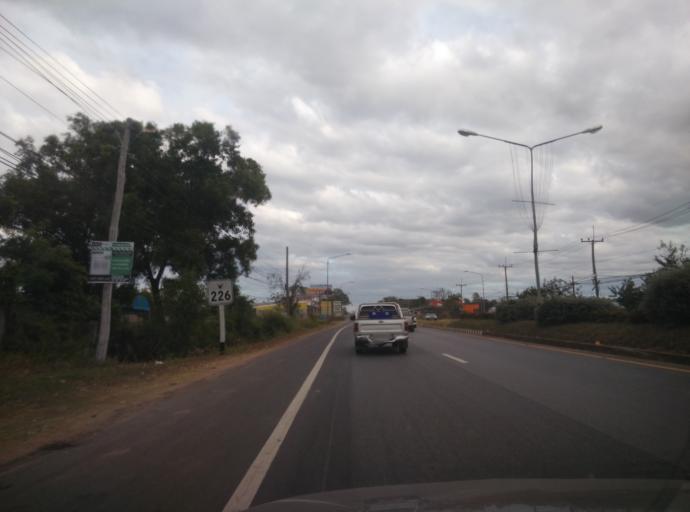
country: TH
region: Sisaket
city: Si Sa Ket
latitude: 15.1264
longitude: 104.2853
